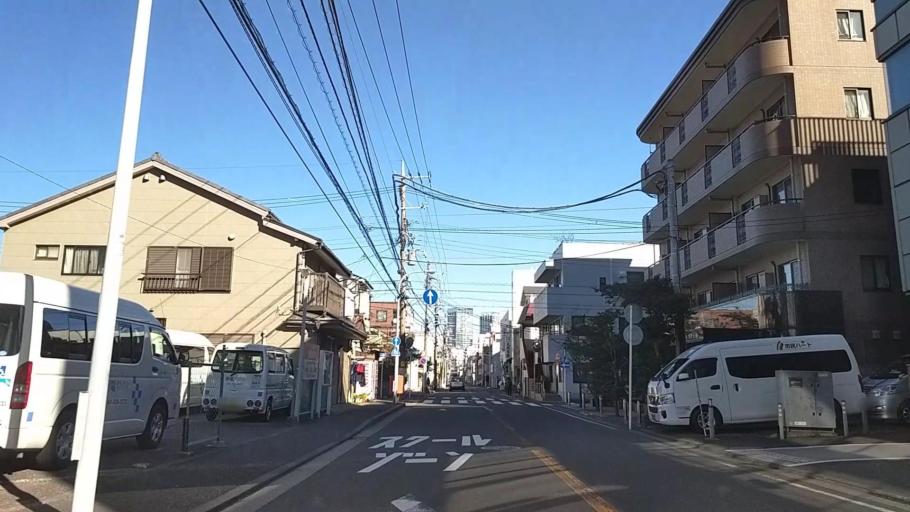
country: JP
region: Kanagawa
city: Yokohama
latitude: 35.4595
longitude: 139.6122
